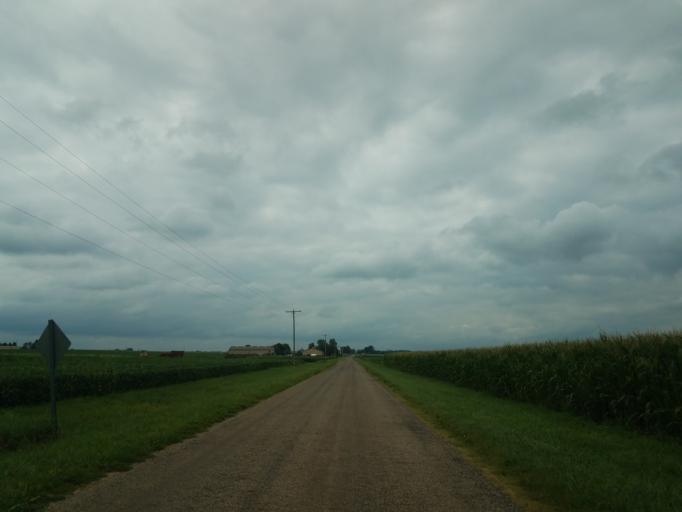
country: US
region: Illinois
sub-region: McLean County
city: Twin Grove
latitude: 40.4349
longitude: -89.0625
